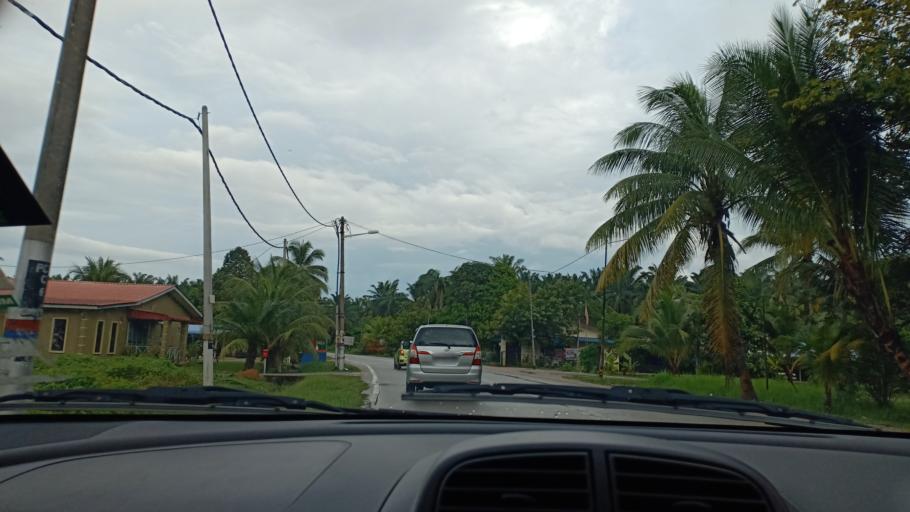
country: MY
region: Penang
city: Tasek Glugor
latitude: 5.4482
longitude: 100.4820
